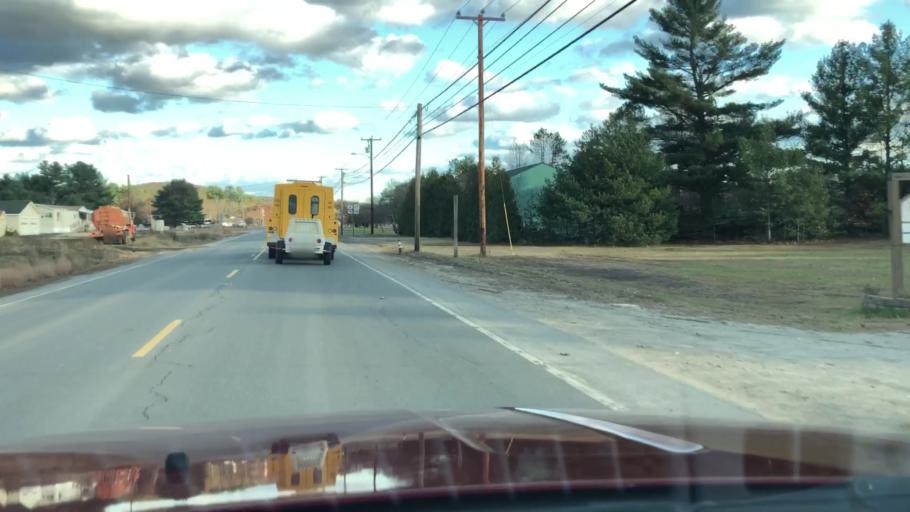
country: US
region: Maine
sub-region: Oxford County
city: Peru
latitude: 44.5179
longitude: -70.4139
